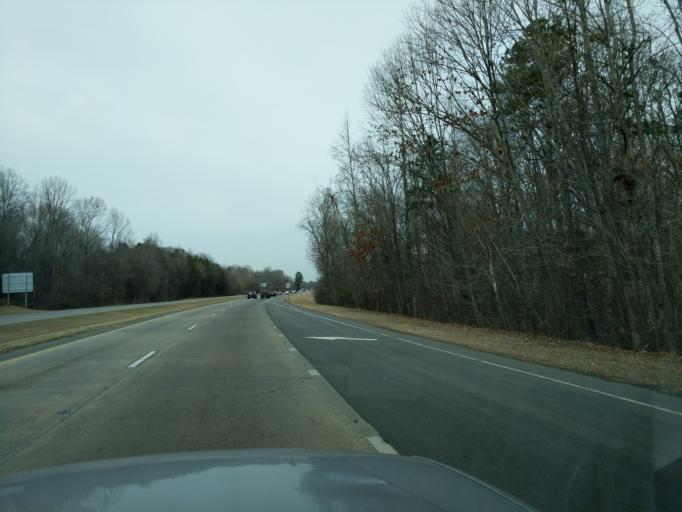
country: US
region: North Carolina
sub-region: Mecklenburg County
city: Charlotte
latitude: 35.1981
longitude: -80.9212
